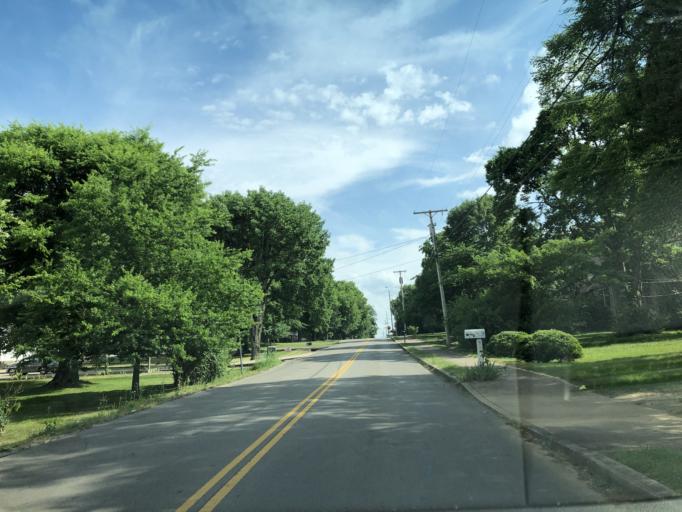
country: US
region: Tennessee
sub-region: Davidson County
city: Goodlettsville
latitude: 36.2724
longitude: -86.7028
